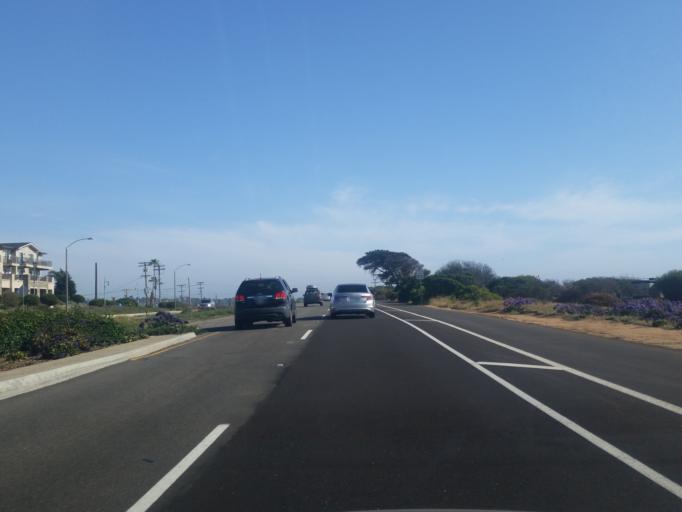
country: US
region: California
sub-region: San Diego County
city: Encinitas
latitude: 33.0975
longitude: -117.3167
